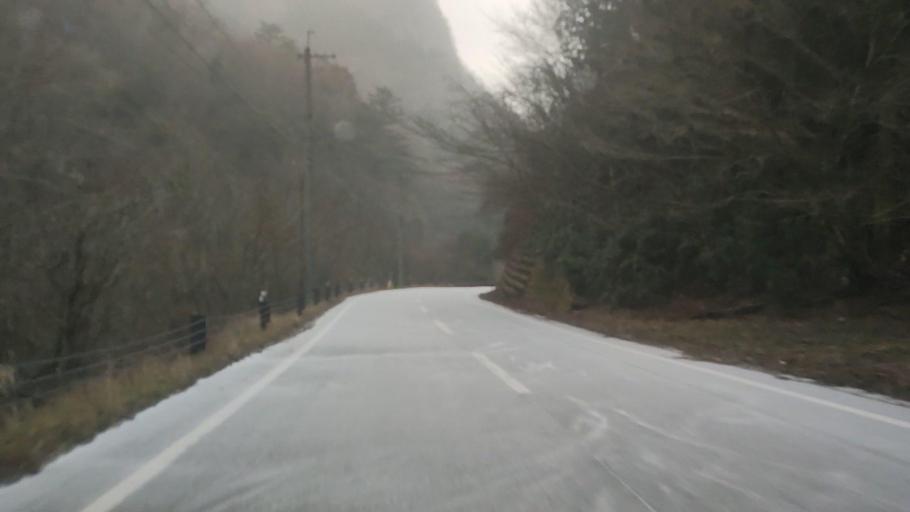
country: JP
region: Kumamoto
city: Matsubase
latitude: 32.5593
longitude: 130.9178
